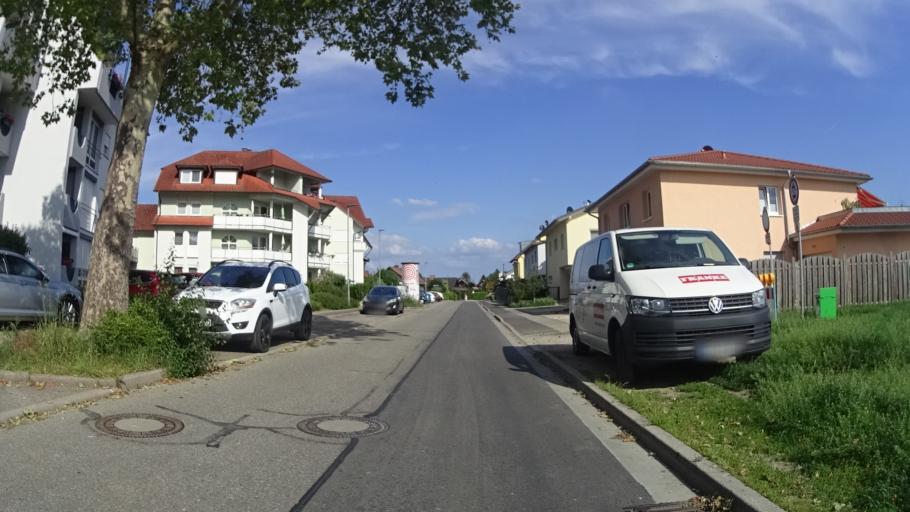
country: DE
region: Baden-Wuerttemberg
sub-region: Freiburg Region
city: Breisach am Rhein
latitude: 48.0416
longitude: 7.5827
